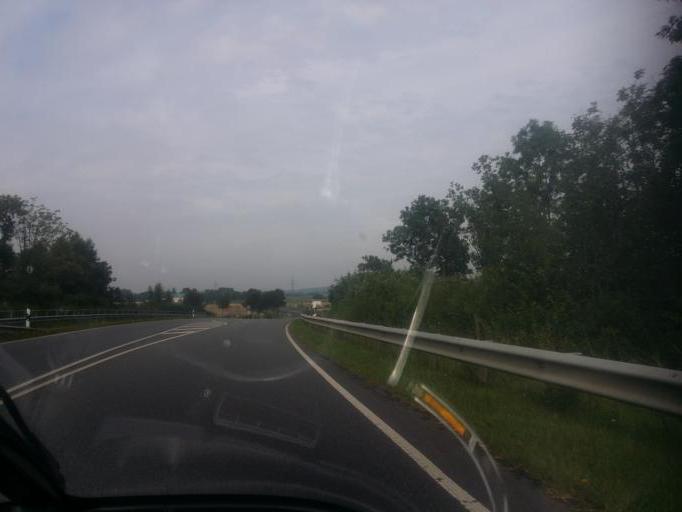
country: DE
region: Schleswig-Holstein
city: Eddelak
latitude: 53.9247
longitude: 9.1550
